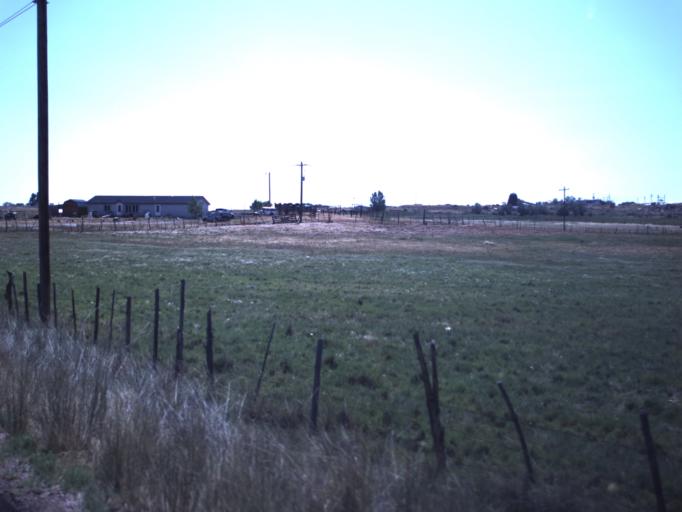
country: US
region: Utah
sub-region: Duchesne County
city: Roosevelt
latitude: 40.4037
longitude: -109.8277
